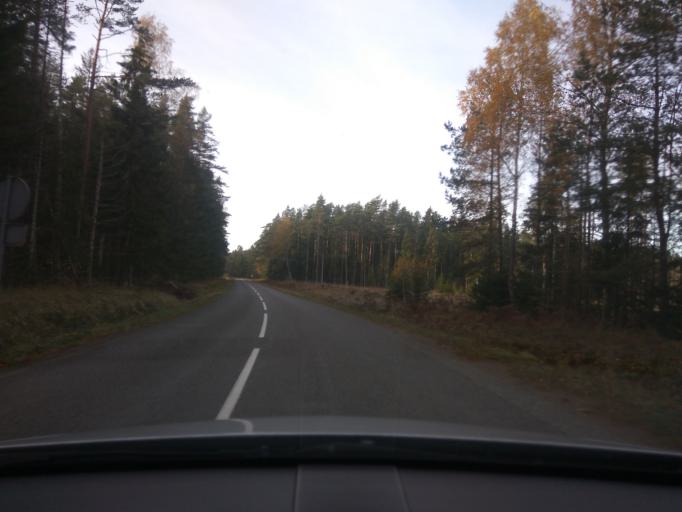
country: LV
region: Alsunga
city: Alsunga
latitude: 57.0135
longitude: 21.4346
